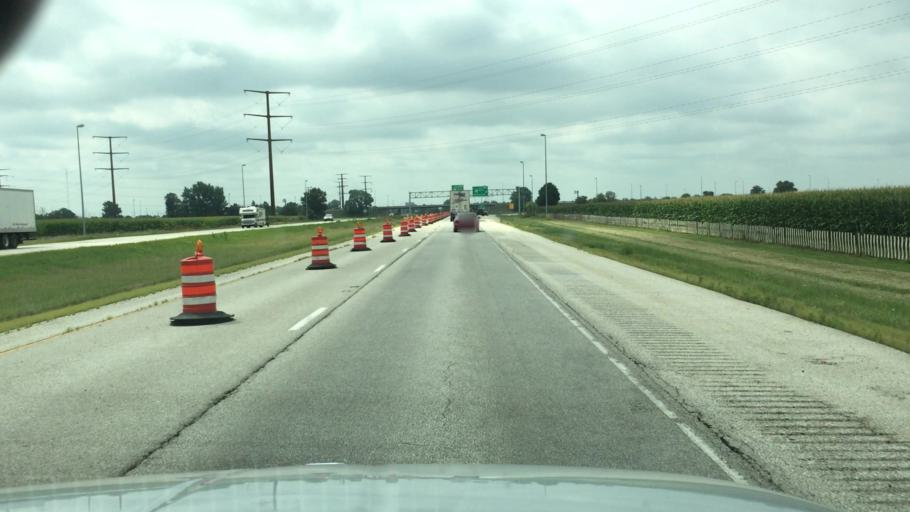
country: US
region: Illinois
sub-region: Knox County
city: Galesburg
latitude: 40.9895
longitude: -90.3363
